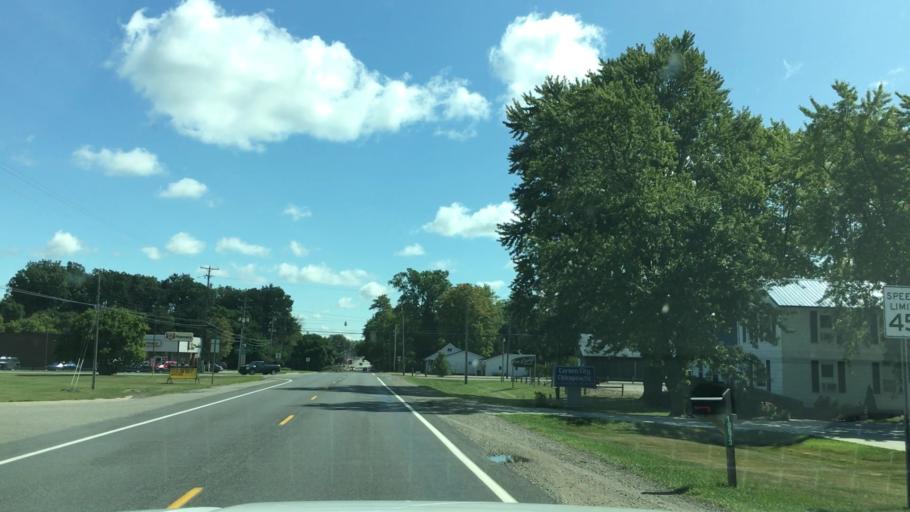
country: US
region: Michigan
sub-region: Montcalm County
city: Carson City
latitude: 43.1772
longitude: -84.8626
